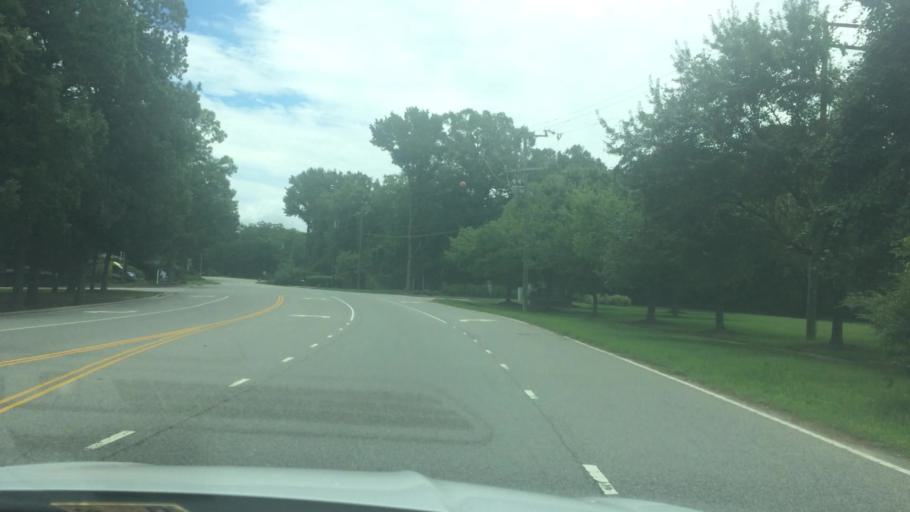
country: US
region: Virginia
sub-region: James City County
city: Williamsburg
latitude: 37.2506
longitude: -76.7651
